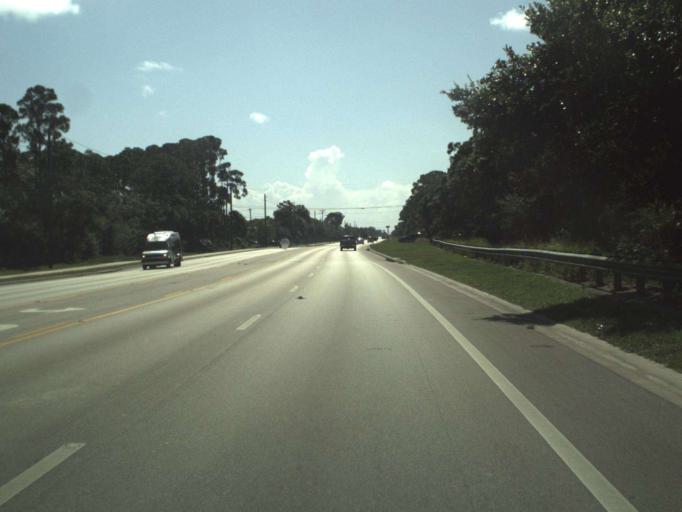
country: US
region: Florida
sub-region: Indian River County
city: Vero Beach South
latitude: 27.5872
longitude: -80.4259
